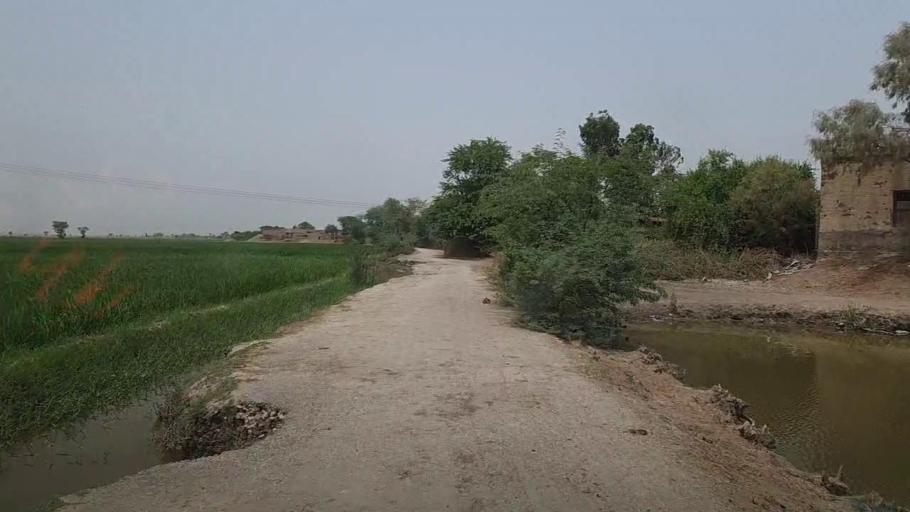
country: PK
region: Sindh
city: Sita Road
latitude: 27.0662
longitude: 67.8484
